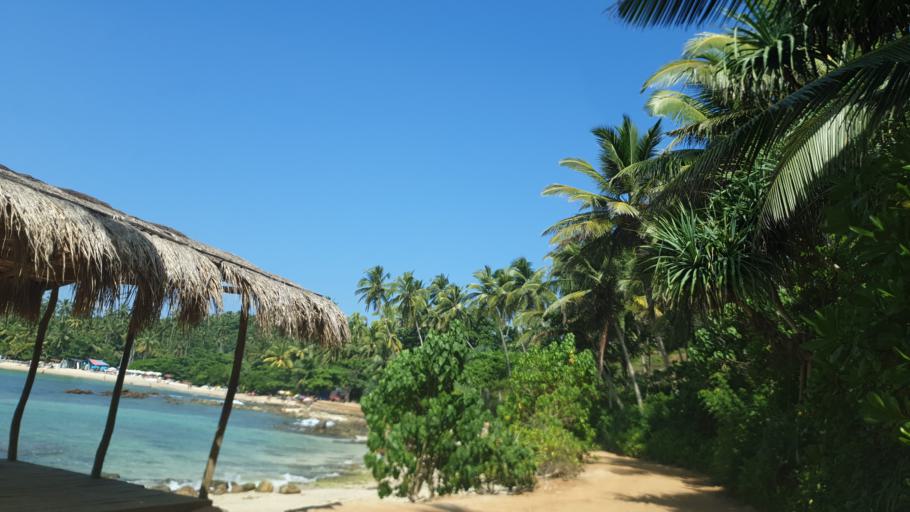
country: LK
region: Southern
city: Tangalla
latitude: 5.9618
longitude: 80.7098
